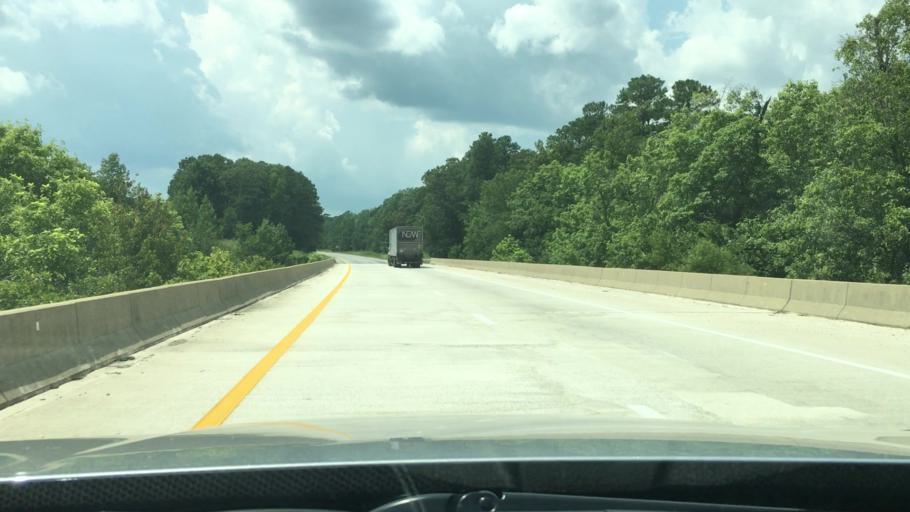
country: US
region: Virginia
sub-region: City of Emporia
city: Emporia
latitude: 36.7643
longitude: -77.4880
